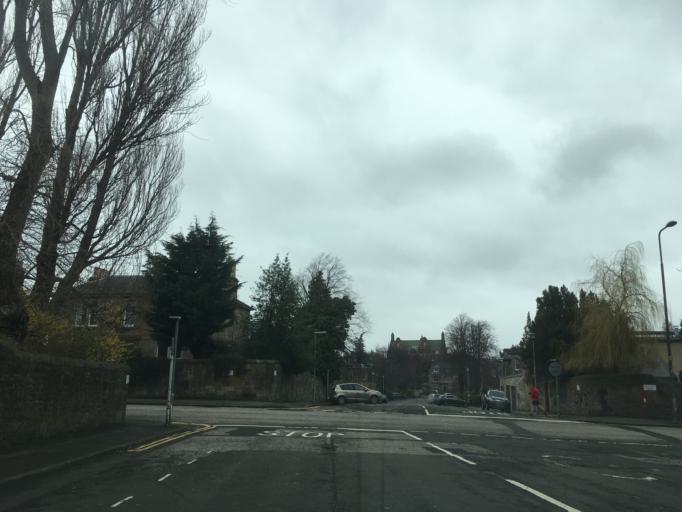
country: GB
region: Scotland
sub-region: Edinburgh
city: Edinburgh
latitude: 55.9355
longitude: -3.1875
